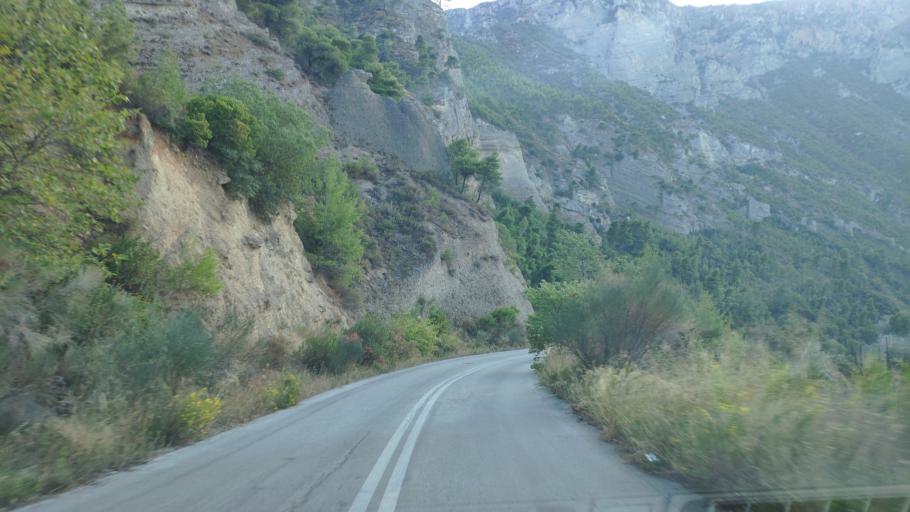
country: GR
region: West Greece
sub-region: Nomos Achaias
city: Aiyira
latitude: 38.0962
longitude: 22.4055
